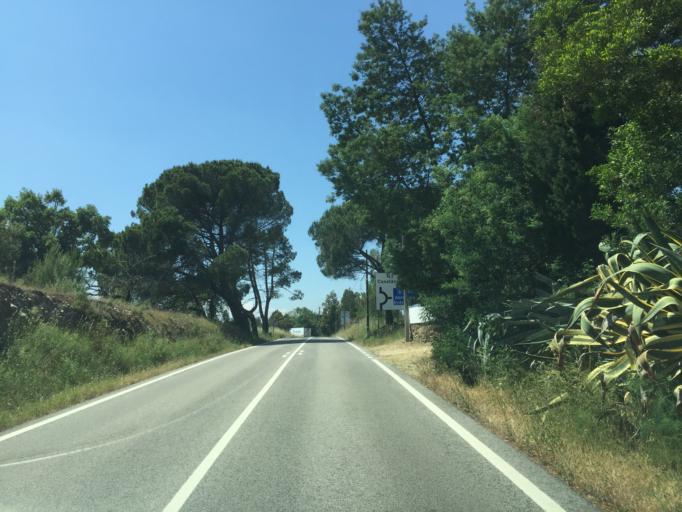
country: PT
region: Santarem
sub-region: Constancia
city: Constancia
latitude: 39.4818
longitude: -8.3228
